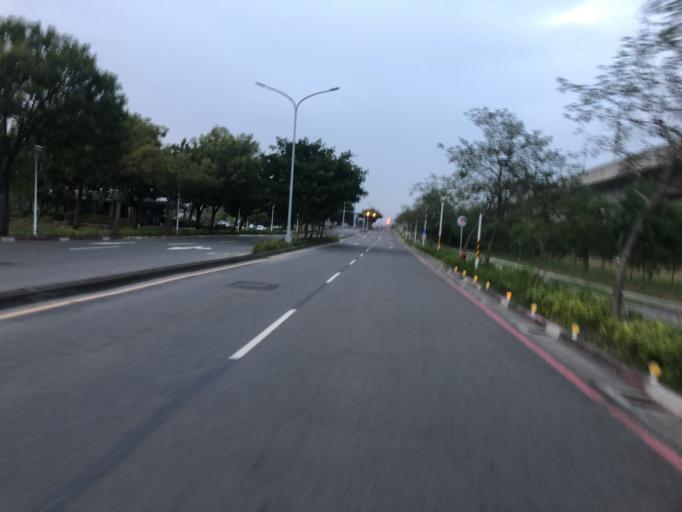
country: TW
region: Taiwan
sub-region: Tainan
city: Tainan
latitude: 23.0878
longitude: 120.2865
